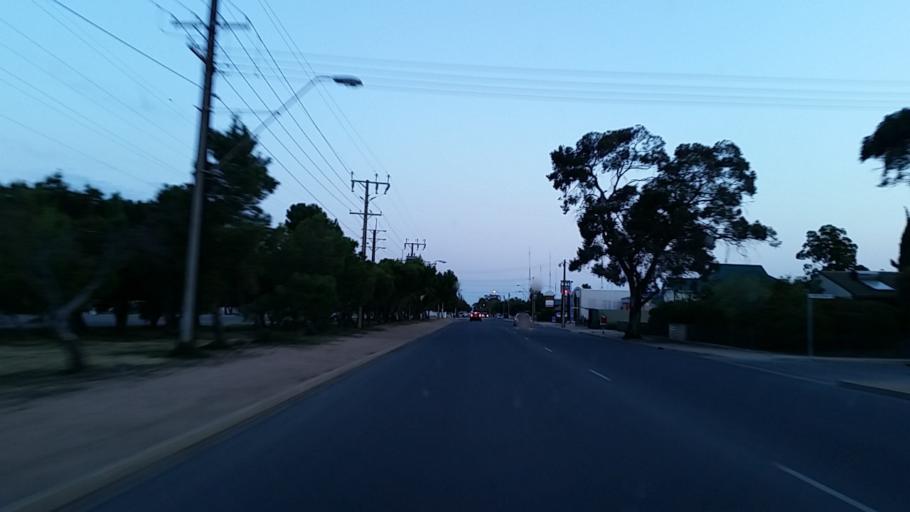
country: AU
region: South Australia
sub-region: Port Pirie City and Dists
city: Port Pirie
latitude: -33.1877
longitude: 138.0039
